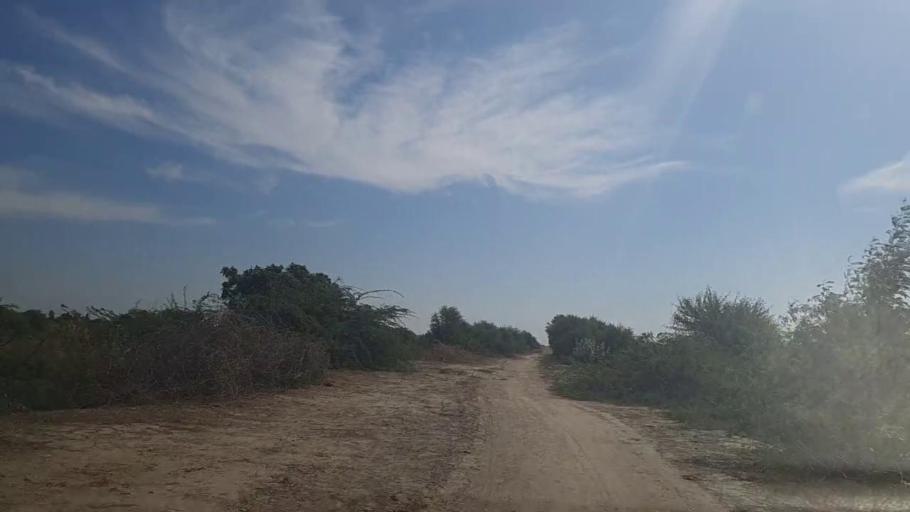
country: PK
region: Sindh
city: Mirpur Batoro
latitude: 24.6546
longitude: 68.2015
